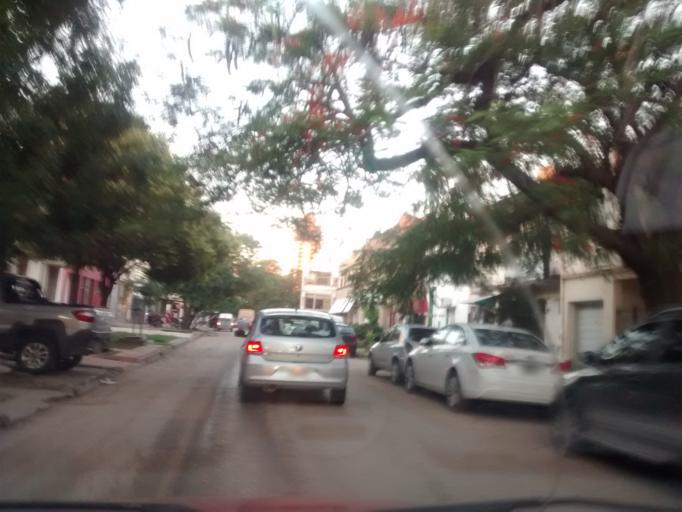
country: AR
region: Chaco
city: Resistencia
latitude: -27.4503
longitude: -58.9924
